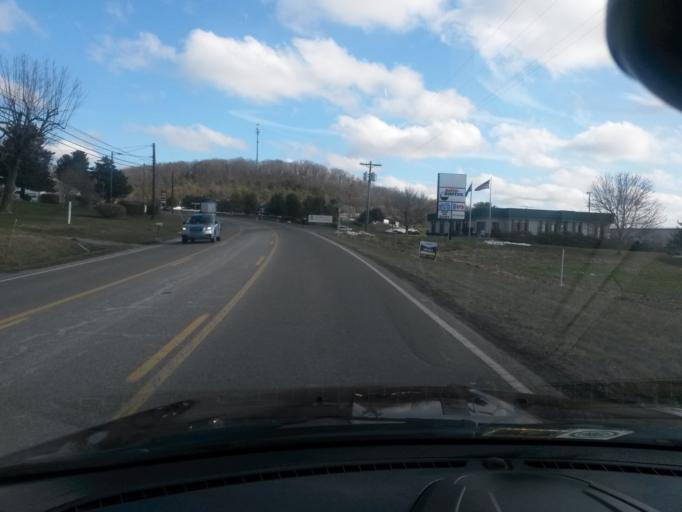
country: US
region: Virginia
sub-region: Augusta County
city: Jolivue
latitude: 38.1040
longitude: -79.0731
